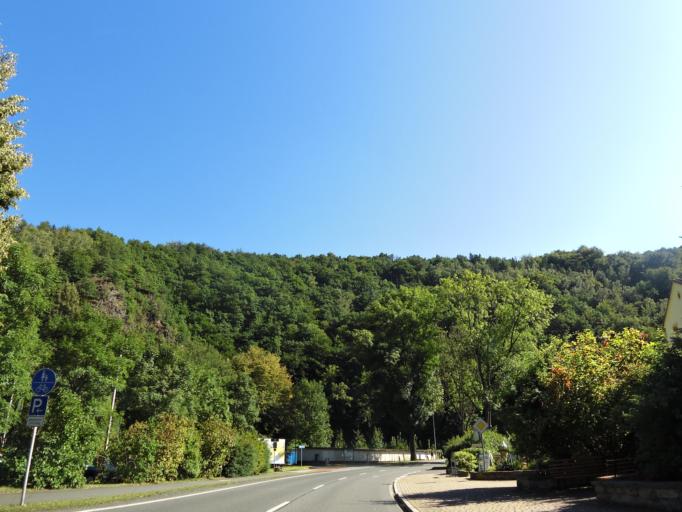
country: DE
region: Saxony
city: Dohna
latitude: 50.9339
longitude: 13.8632
